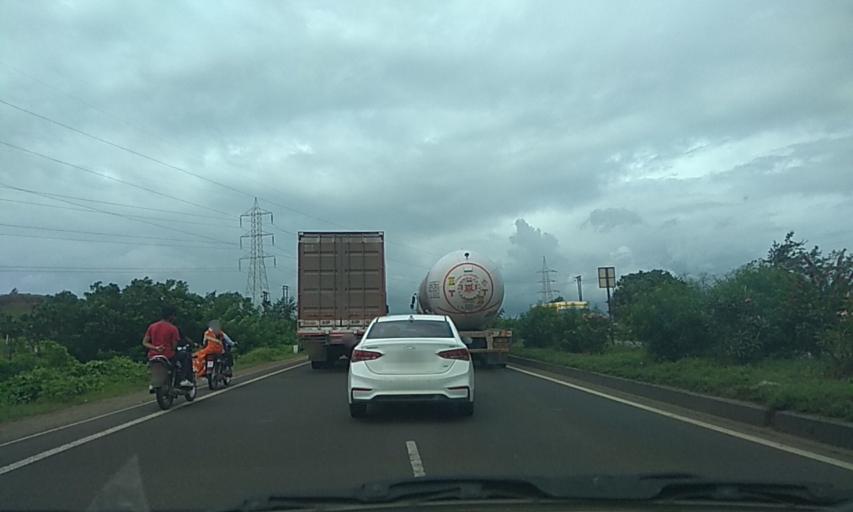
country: IN
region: Maharashtra
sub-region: Kolhapur
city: Kagal
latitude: 16.6050
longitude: 74.3069
